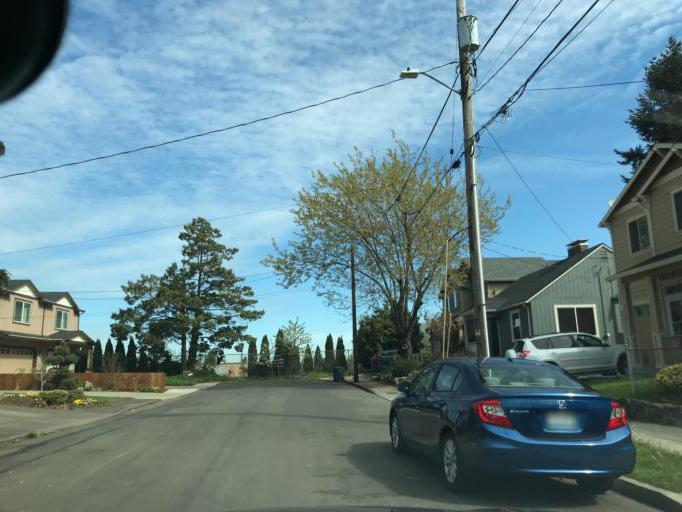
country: US
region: Oregon
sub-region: Multnomah County
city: Lents
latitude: 45.4914
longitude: -122.5715
